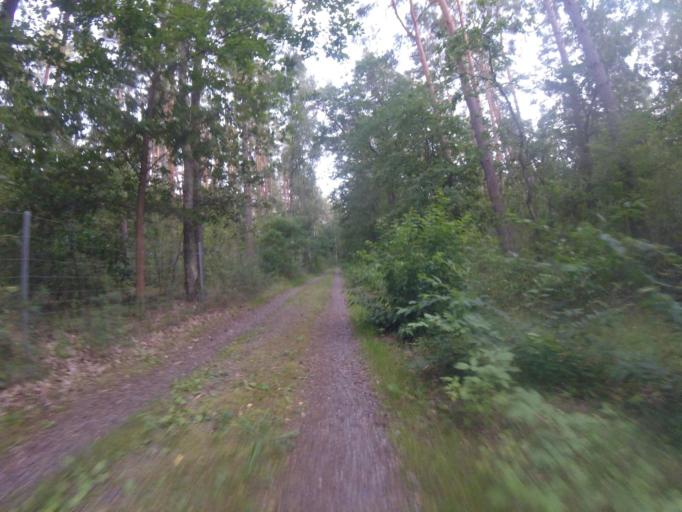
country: DE
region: Berlin
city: Bohnsdorf
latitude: 52.3894
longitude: 13.5930
